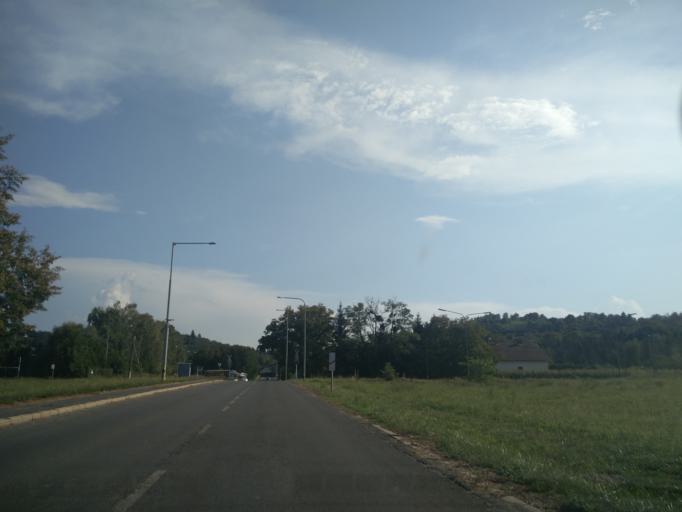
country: HU
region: Zala
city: Zalaegerszeg
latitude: 46.8552
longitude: 16.7988
